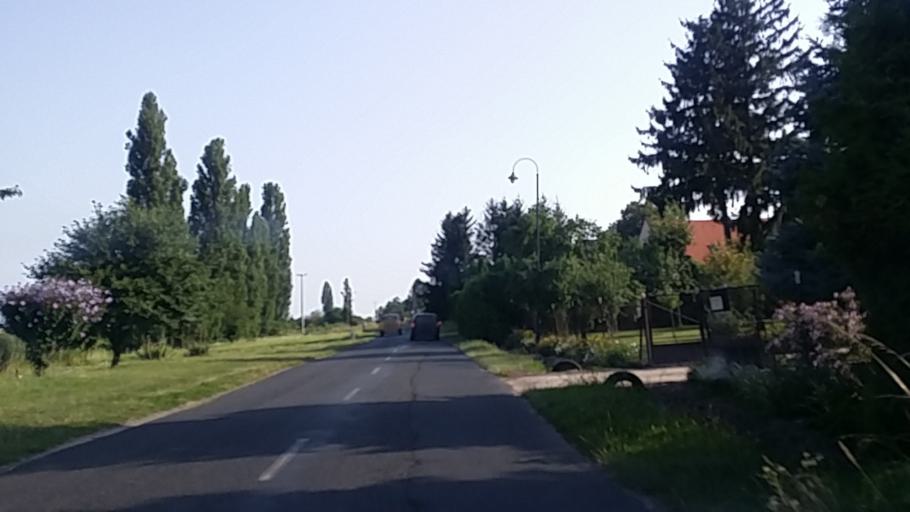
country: HU
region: Veszprem
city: Badacsonytomaj
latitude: 46.7904
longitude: 17.4492
